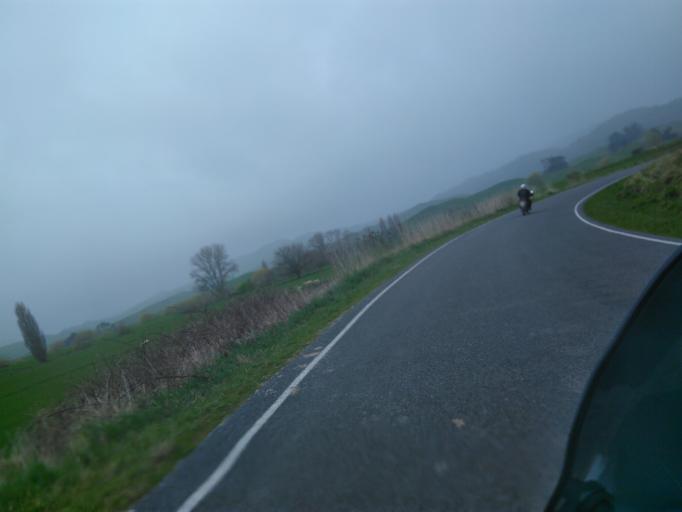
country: NZ
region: Gisborne
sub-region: Gisborne District
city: Gisborne
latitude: -38.6493
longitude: 177.7256
